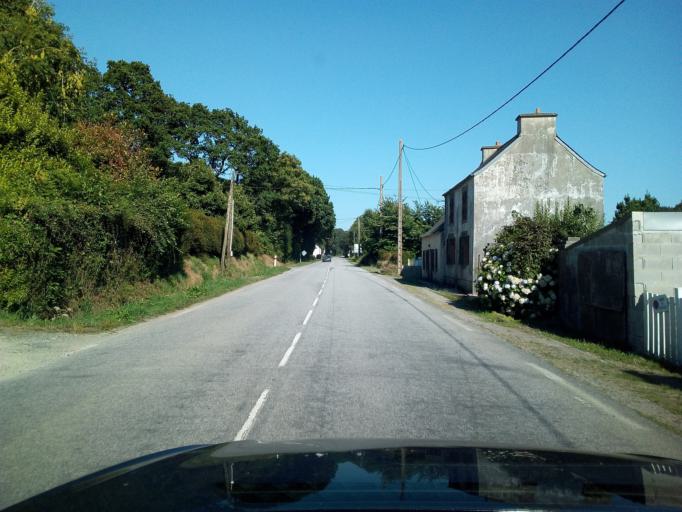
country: FR
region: Brittany
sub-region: Departement du Finistere
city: Landivisiau
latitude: 48.4991
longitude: -4.0979
